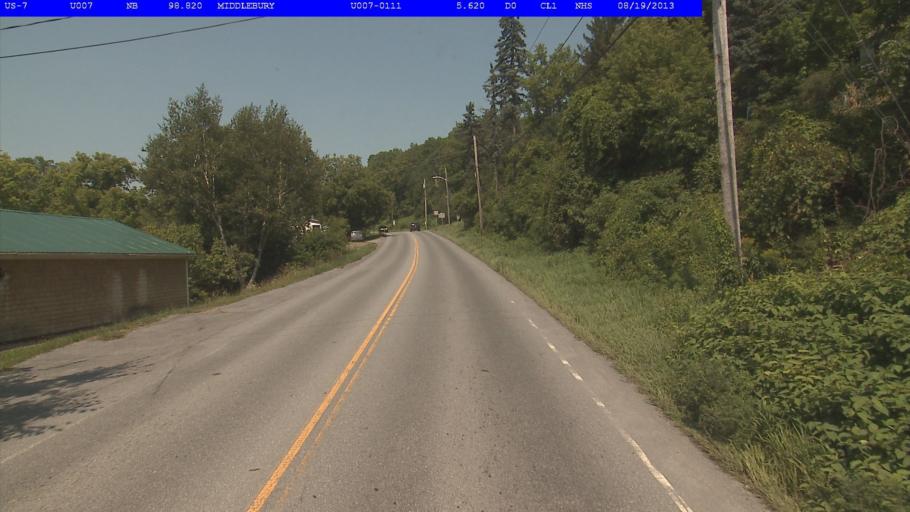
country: US
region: Vermont
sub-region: Addison County
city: Middlebury (village)
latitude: 44.0218
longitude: -73.1653
